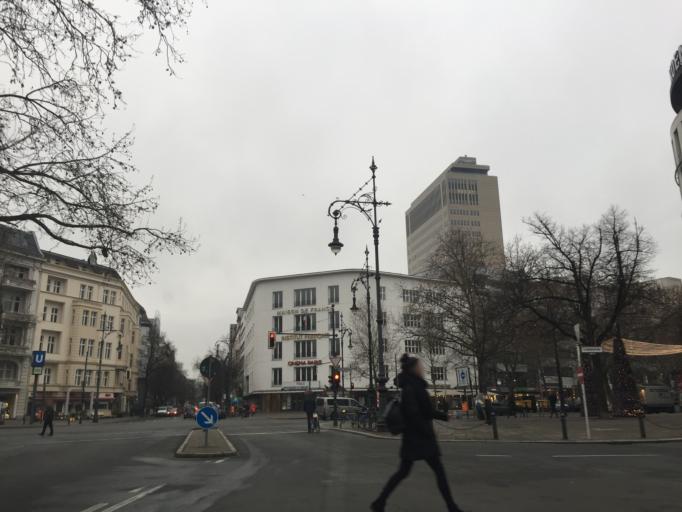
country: DE
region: Berlin
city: Wilmersdorf Bezirk
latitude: 52.5030
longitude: 13.3253
